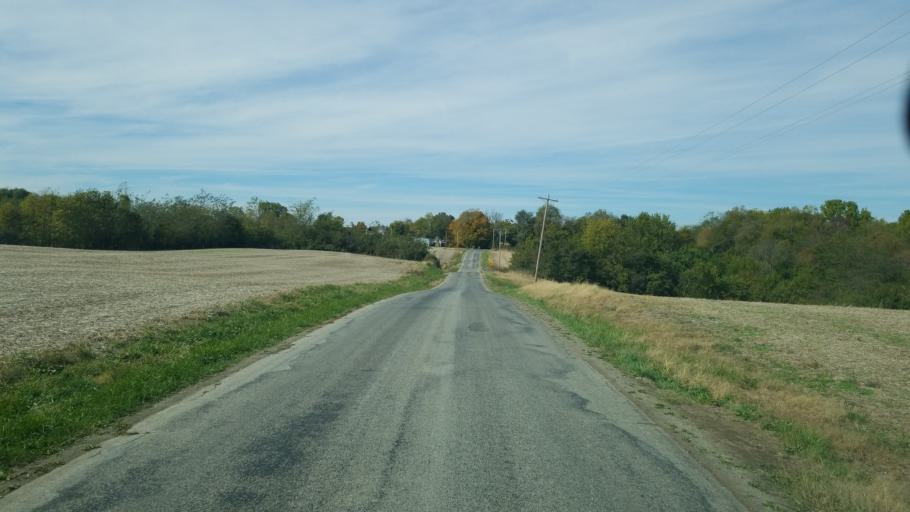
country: US
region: Ohio
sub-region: Highland County
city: Leesburg
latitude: 39.3185
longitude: -83.4703
